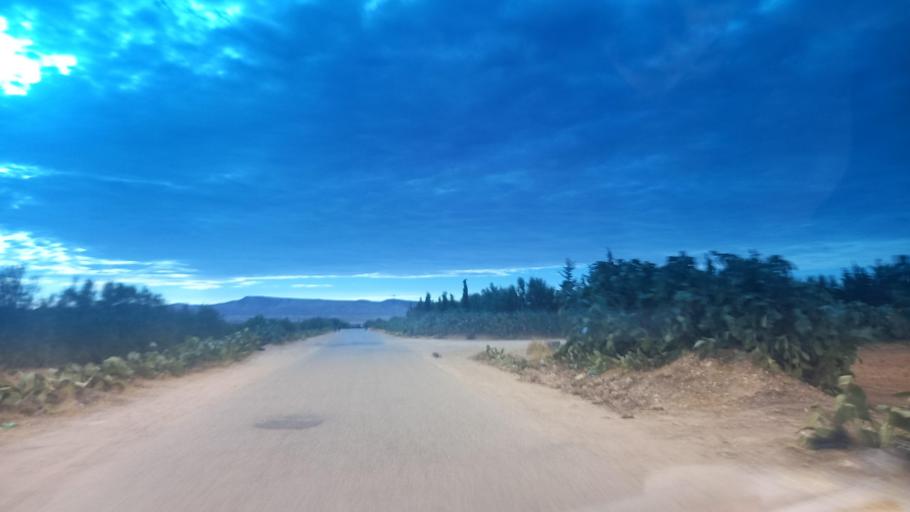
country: TN
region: Al Qasrayn
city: Sbiba
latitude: 35.3801
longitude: 9.0563
